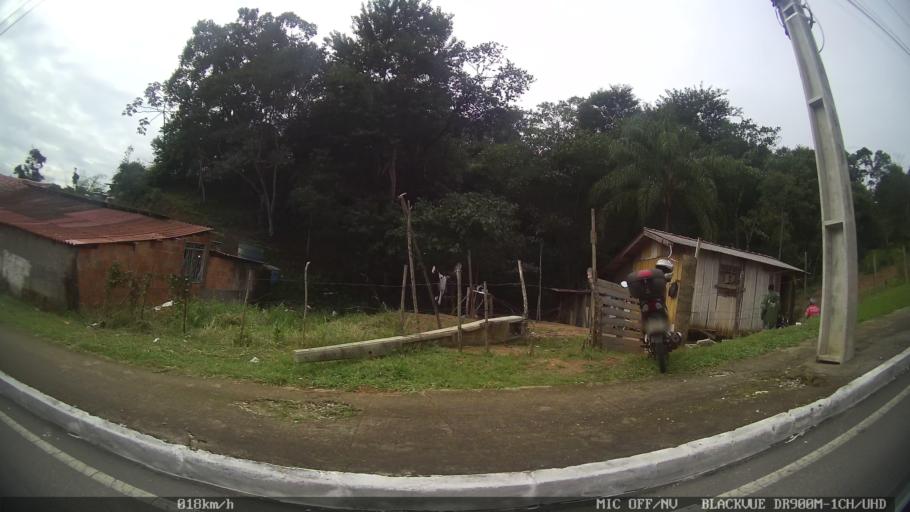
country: BR
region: Santa Catarina
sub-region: Sao Jose
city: Campinas
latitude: -27.5522
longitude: -48.6445
